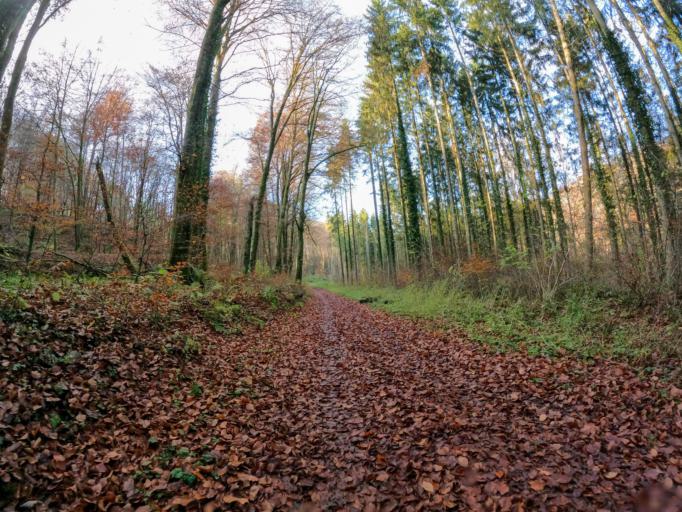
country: LU
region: Luxembourg
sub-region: Canton de Capellen
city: Mamer
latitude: 49.6434
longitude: 6.0268
